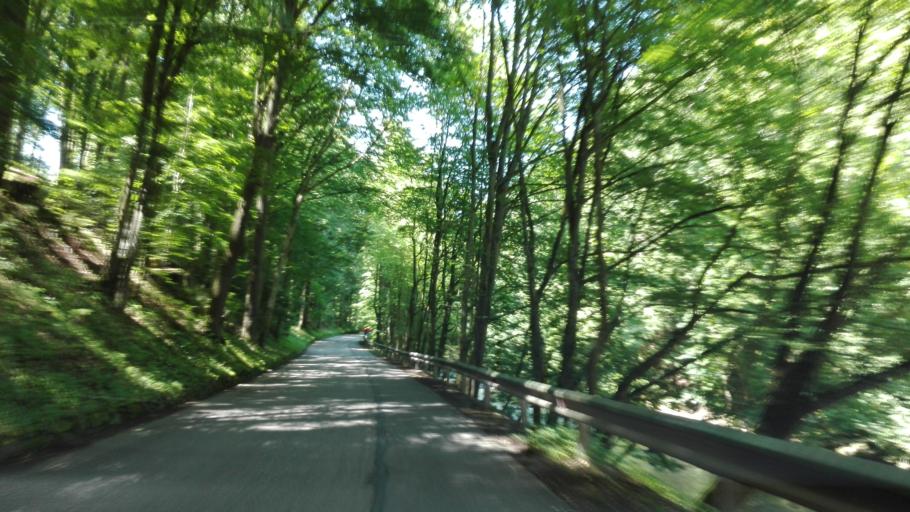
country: AT
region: Upper Austria
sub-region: Politischer Bezirk Rohrbach
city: Kleinzell im Muehlkreis
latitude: 48.3801
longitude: 13.9325
